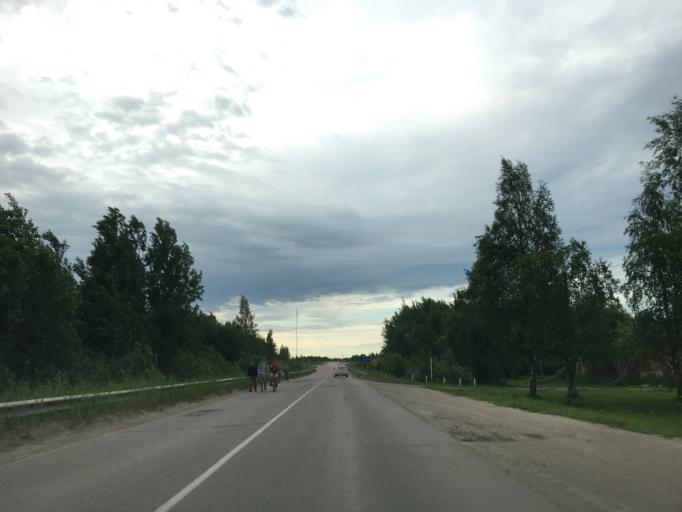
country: RU
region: Pskov
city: Pskov
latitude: 57.8541
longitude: 28.3072
